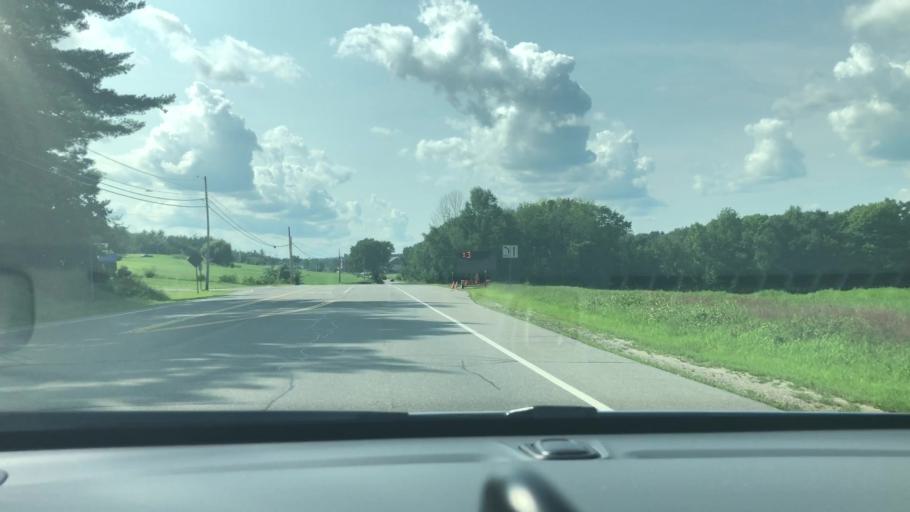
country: US
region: New Hampshire
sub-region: Hillsborough County
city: Pinardville
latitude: 43.0071
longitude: -71.5297
